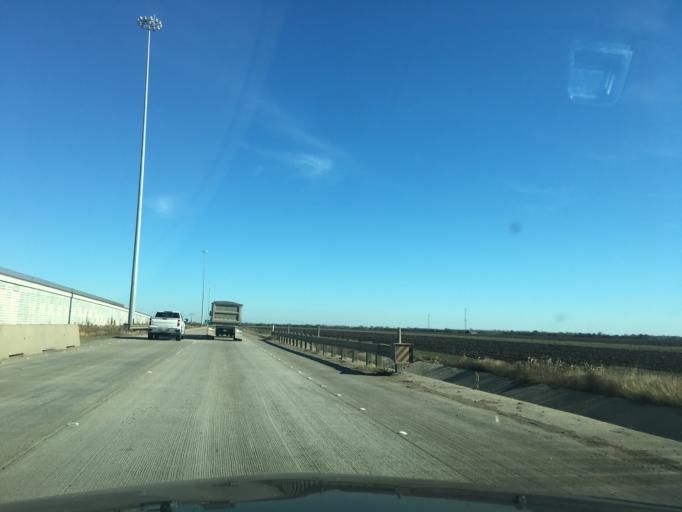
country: US
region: Texas
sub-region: Fort Bend County
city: Rosenberg
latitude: 29.5341
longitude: -95.8456
